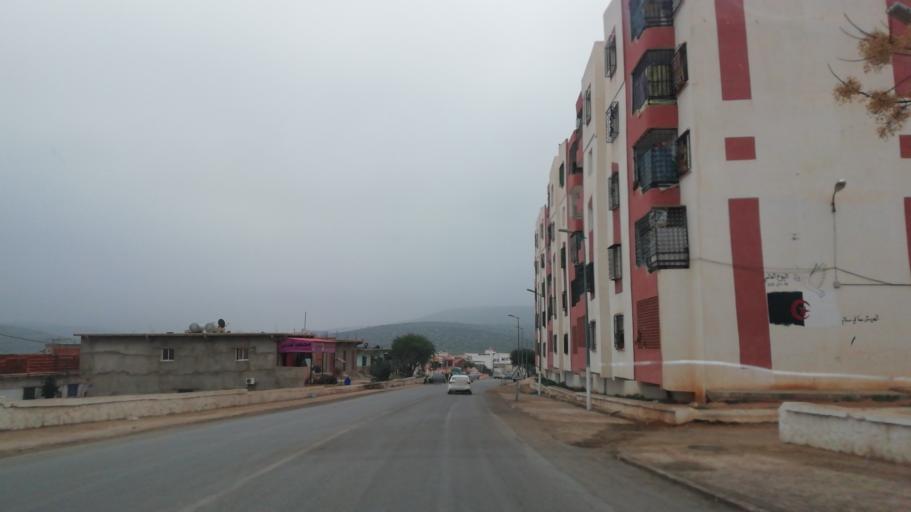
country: DZ
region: Mascara
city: Oued el Abtal
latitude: 35.2909
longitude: 0.4718
